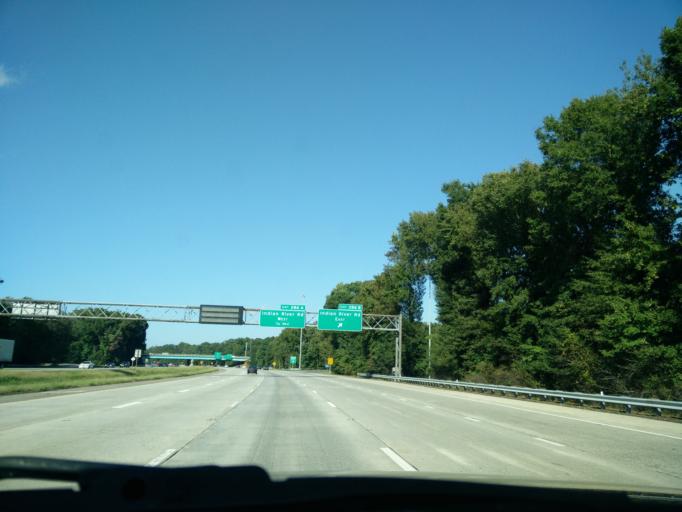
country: US
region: Virginia
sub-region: City of Chesapeake
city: Chesapeake
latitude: 36.8035
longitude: -76.1975
